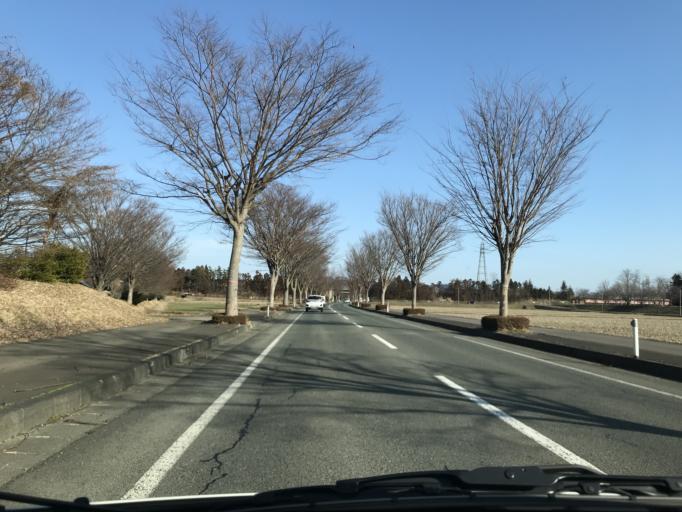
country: JP
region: Iwate
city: Kitakami
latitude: 39.2909
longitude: 141.0804
